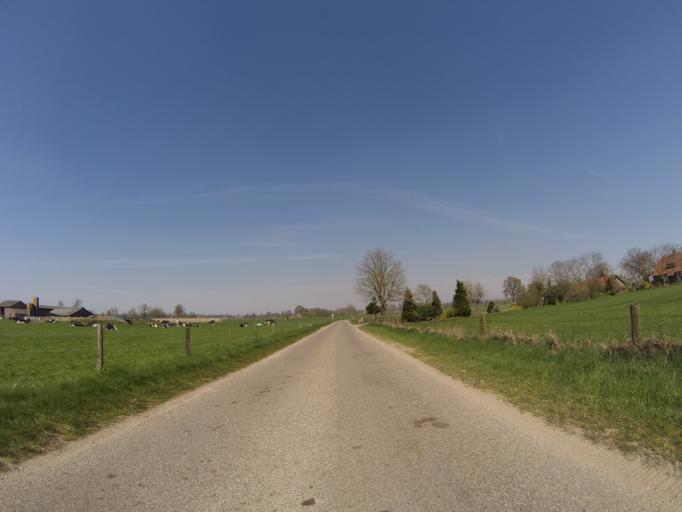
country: NL
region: Utrecht
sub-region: Gemeente Rhenen
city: Rhenen
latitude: 51.9639
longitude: 5.5998
